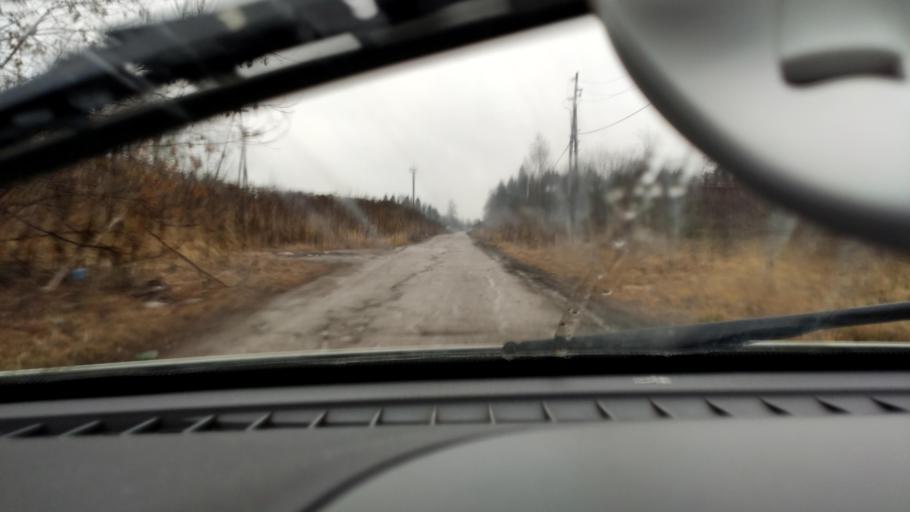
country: RU
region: Perm
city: Perm
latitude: 58.0345
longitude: 56.4110
